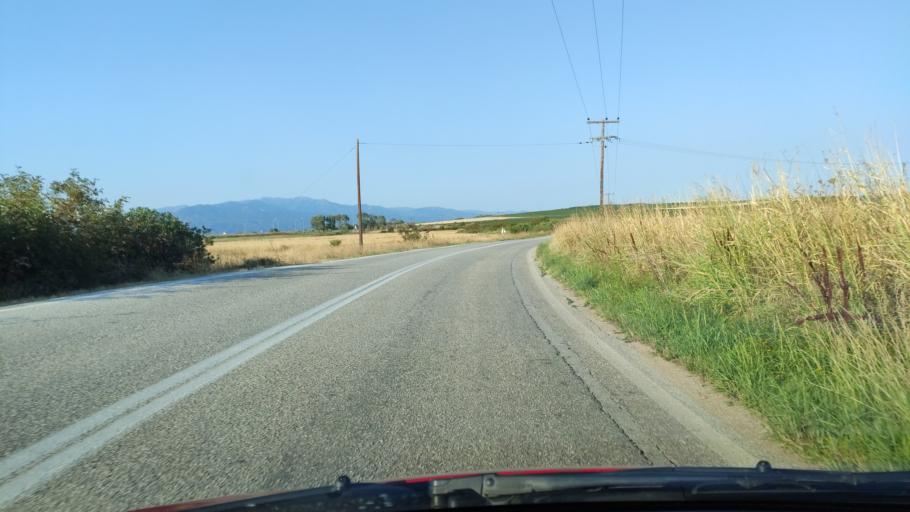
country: GR
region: East Macedonia and Thrace
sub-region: Nomos Rodopis
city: Iasmos
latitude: 40.9983
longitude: 25.1709
